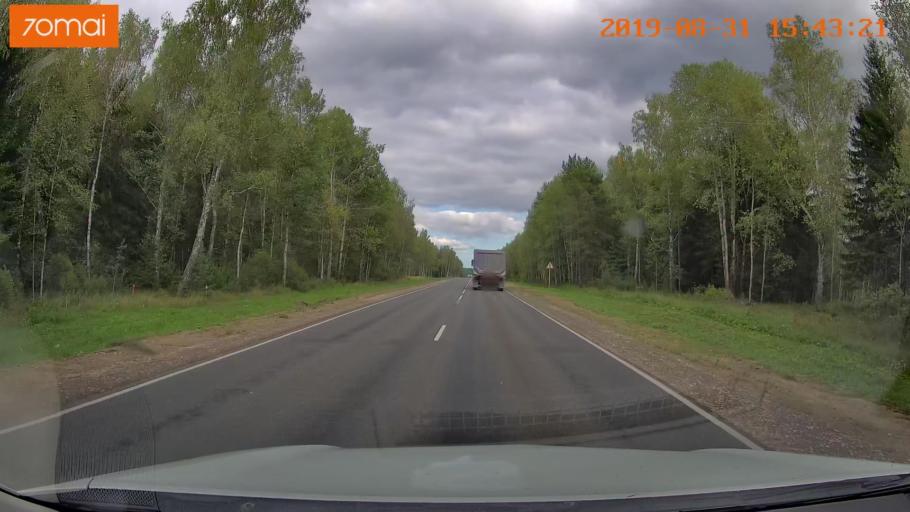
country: RU
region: Kaluga
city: Mosal'sk
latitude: 54.6525
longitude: 34.9088
